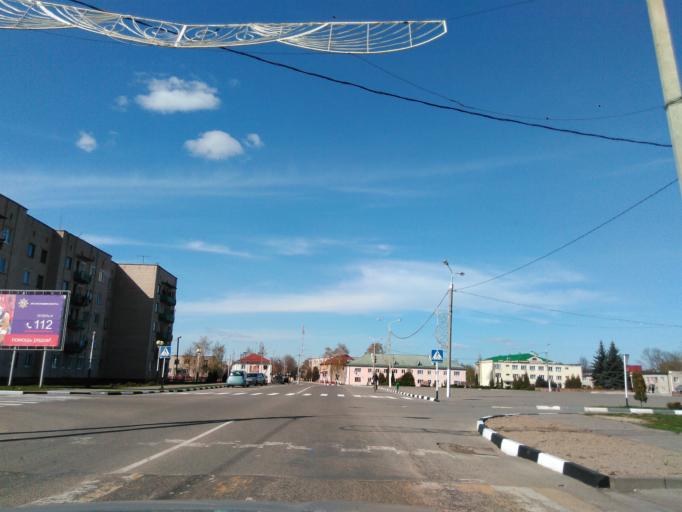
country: BY
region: Vitebsk
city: Chashniki
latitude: 54.8562
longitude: 29.1592
